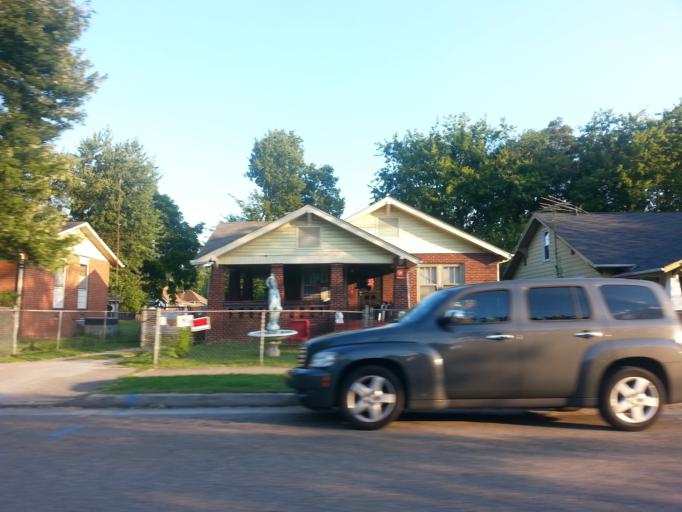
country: US
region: Tennessee
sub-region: Knox County
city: Knoxville
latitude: 35.9776
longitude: -83.9034
